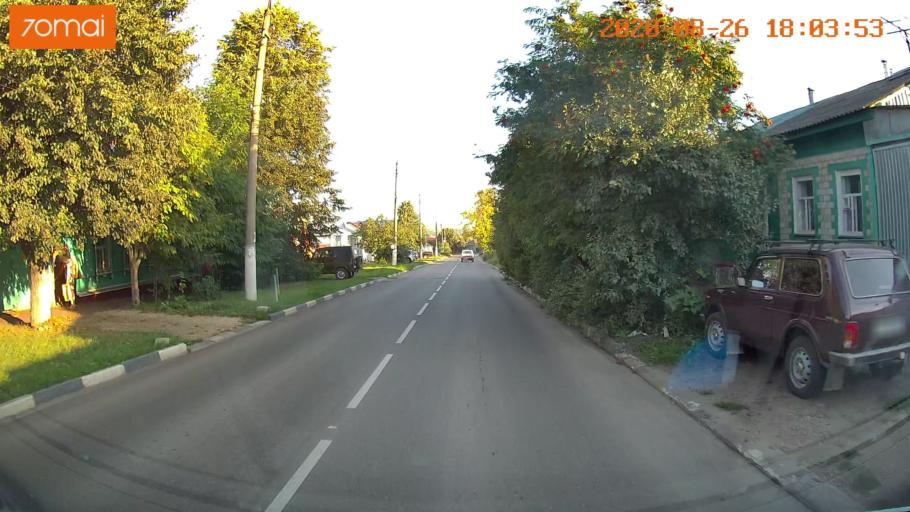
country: RU
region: Tula
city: Yefremov
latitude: 53.1400
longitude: 38.1134
